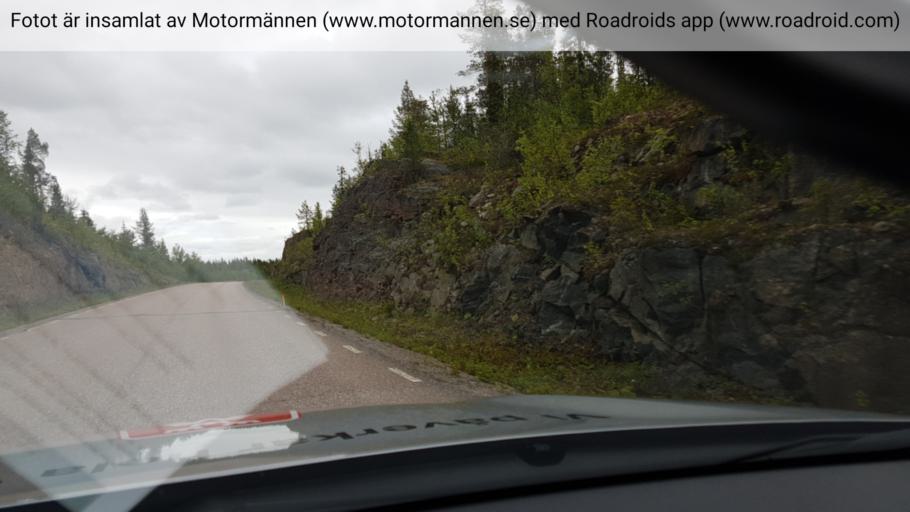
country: SE
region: Norrbotten
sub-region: Overkalix Kommun
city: OEverkalix
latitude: 67.0450
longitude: 22.0609
